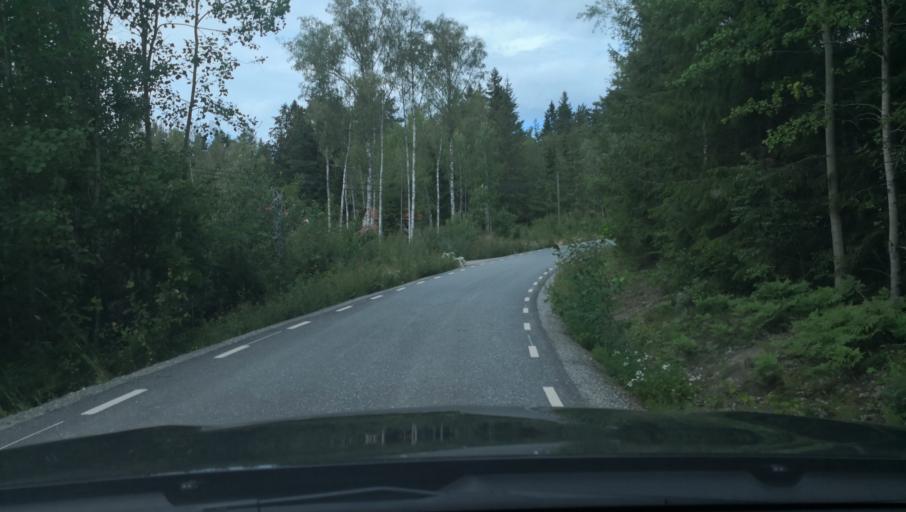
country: SE
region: Vaestmanland
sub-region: Hallstahammars Kommun
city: Hallstahammar
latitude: 59.6239
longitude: 16.1428
